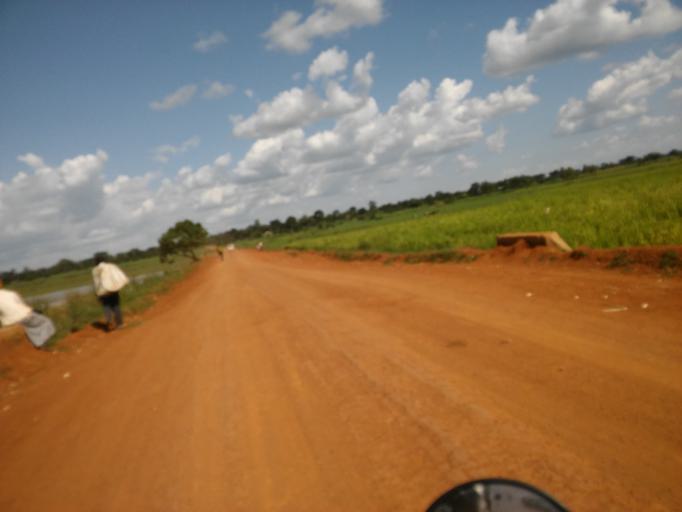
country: UG
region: Eastern Region
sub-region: Pallisa District
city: Pallisa
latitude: 1.1360
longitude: 33.7275
